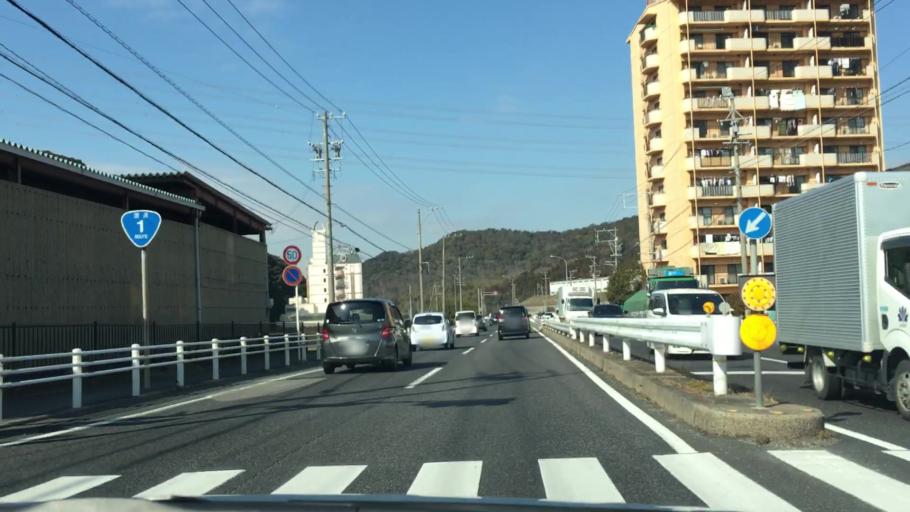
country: JP
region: Aichi
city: Gamagori
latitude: 34.9033
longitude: 137.2353
